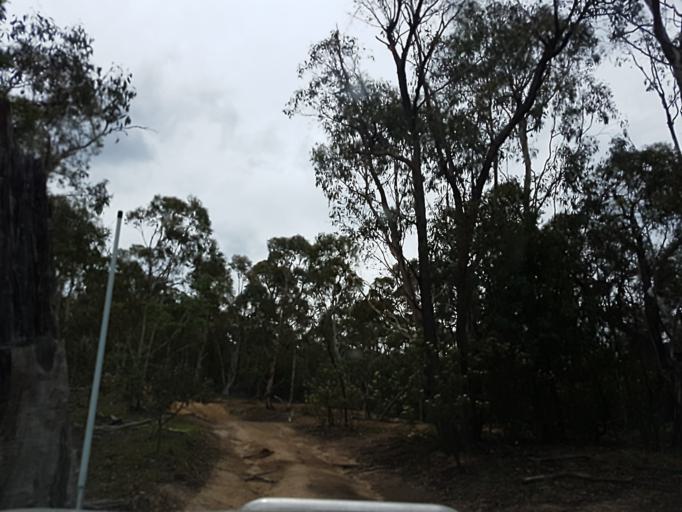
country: AU
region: New South Wales
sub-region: Snowy River
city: Jindabyne
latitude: -36.8910
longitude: 148.3380
